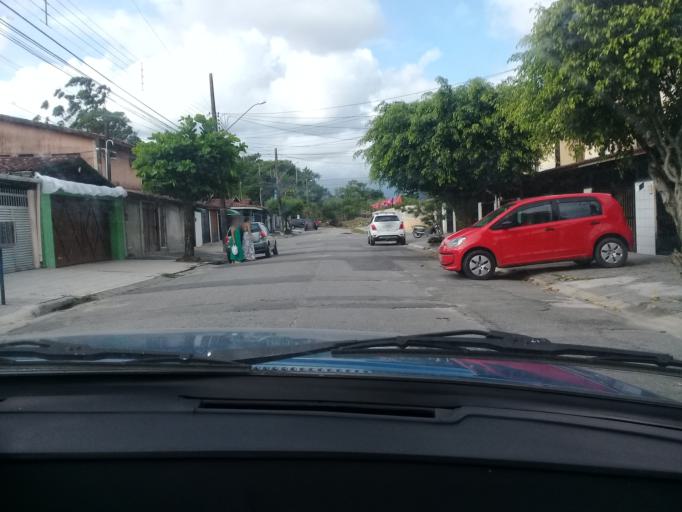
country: BR
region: Sao Paulo
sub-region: Guaruja
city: Guaruja
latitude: -23.9887
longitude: -46.2814
